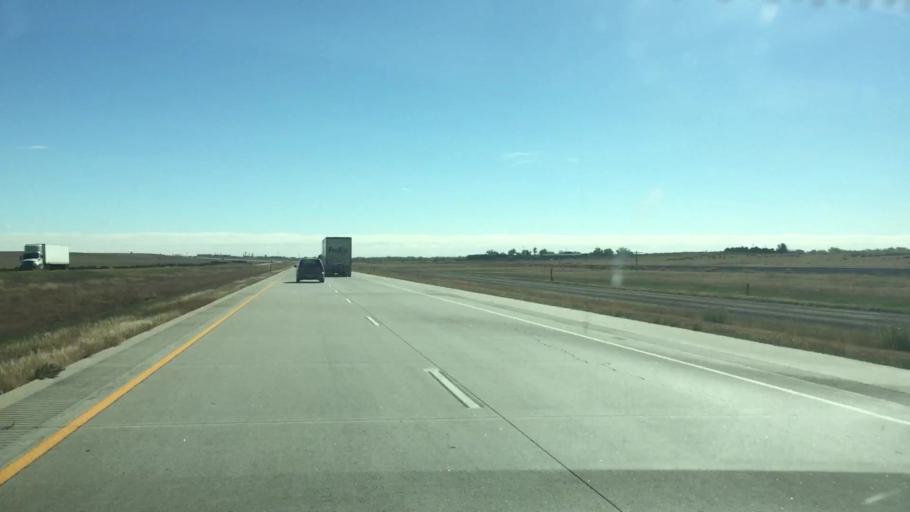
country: US
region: Colorado
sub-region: Lincoln County
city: Limon
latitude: 39.2778
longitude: -103.7561
